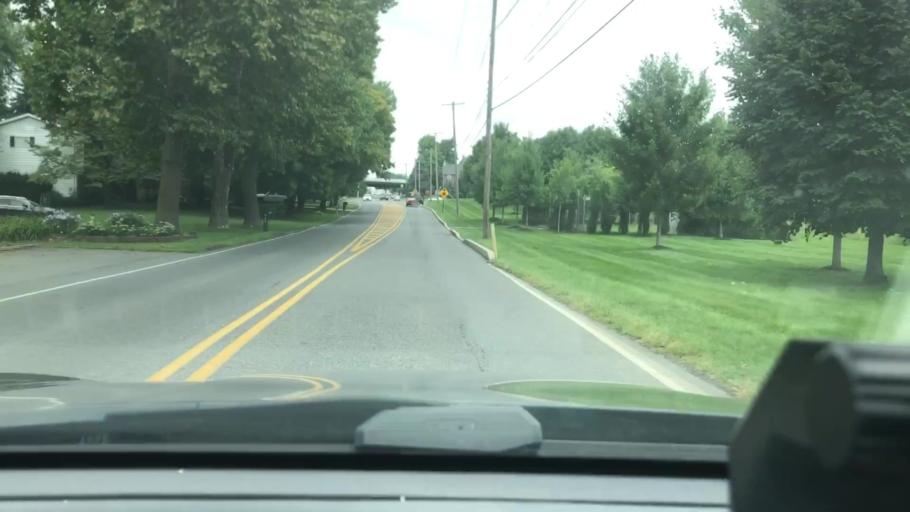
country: US
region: Pennsylvania
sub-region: Lehigh County
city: Fullerton
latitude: 40.6350
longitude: -75.4466
